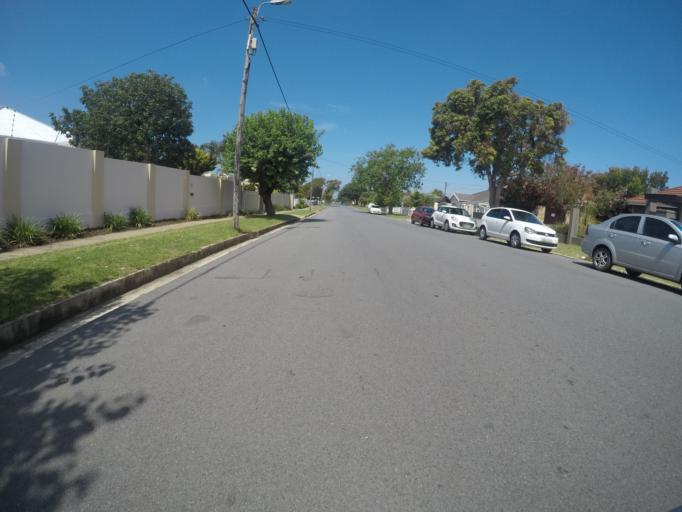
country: ZA
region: Eastern Cape
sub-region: Buffalo City Metropolitan Municipality
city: East London
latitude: -32.9789
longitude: 27.9066
